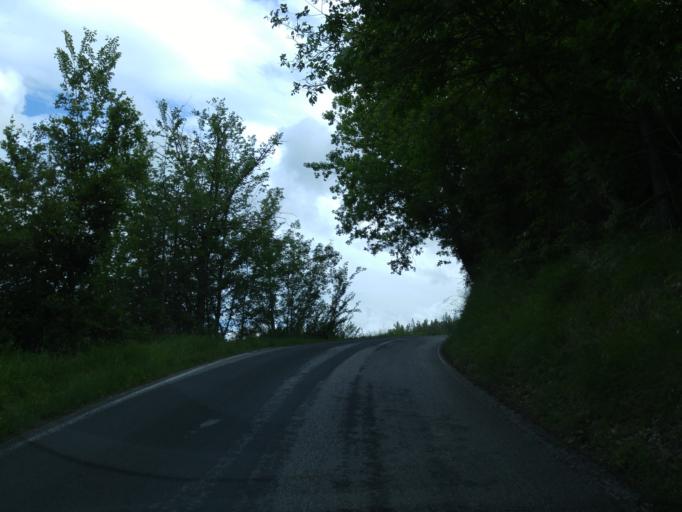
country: IT
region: The Marches
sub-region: Provincia di Pesaro e Urbino
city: Fermignano
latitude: 43.7020
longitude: 12.6372
